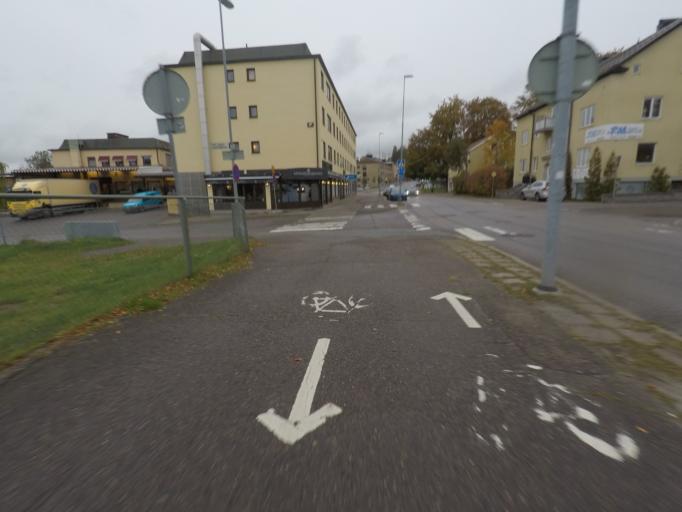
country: SE
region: OErebro
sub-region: Karlskoga Kommun
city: Karlskoga
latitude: 59.3270
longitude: 14.5283
